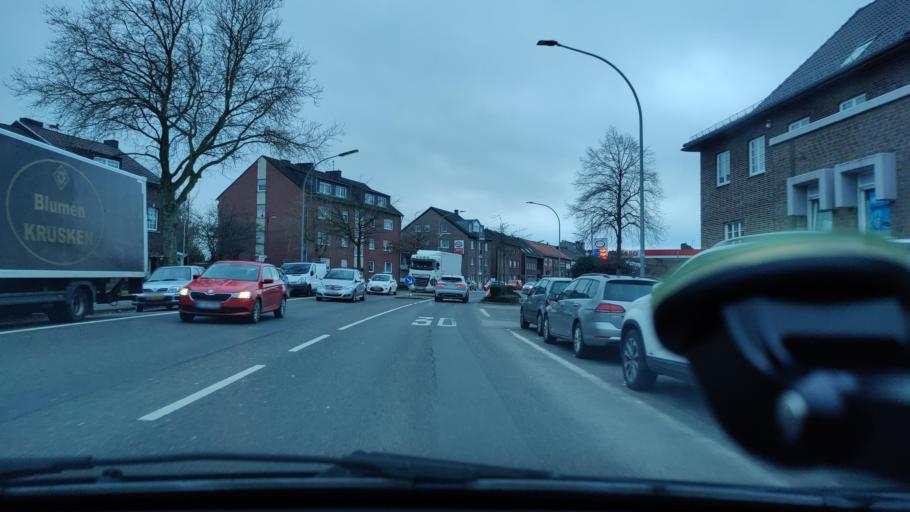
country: DE
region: North Rhine-Westphalia
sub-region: Regierungsbezirk Koln
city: Wurselen
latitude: 50.8214
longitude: 6.1259
